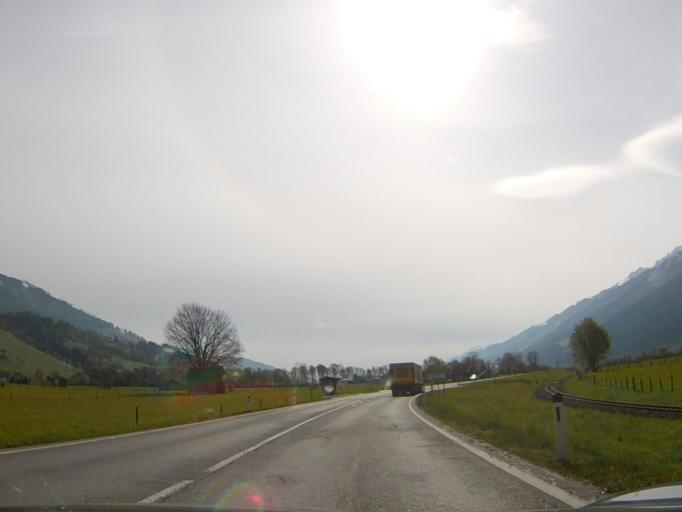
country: AT
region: Salzburg
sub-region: Politischer Bezirk Zell am See
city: Uttendorf
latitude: 47.2842
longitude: 12.5468
